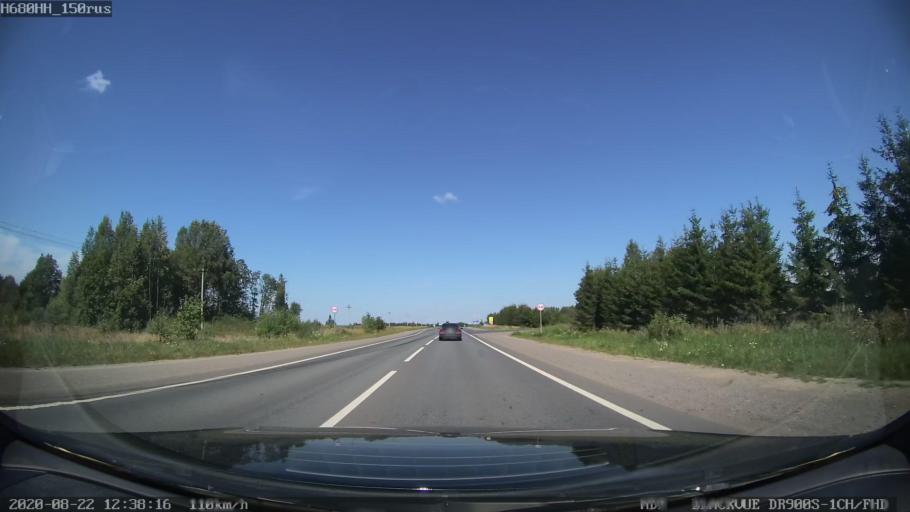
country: RU
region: Tverskaya
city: Rameshki
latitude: 57.3114
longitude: 36.0885
